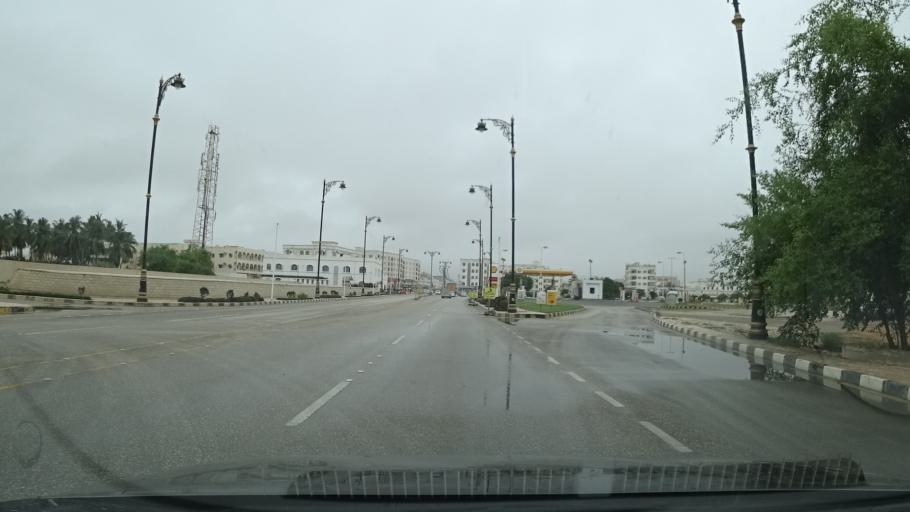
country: OM
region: Zufar
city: Salalah
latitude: 17.0079
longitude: 54.0957
